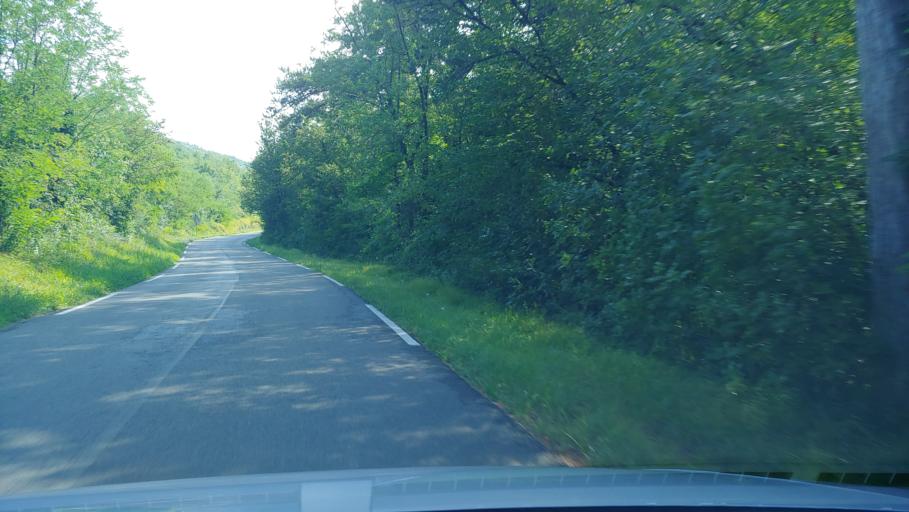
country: SI
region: Komen
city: Komen
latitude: 45.8397
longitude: 13.7669
